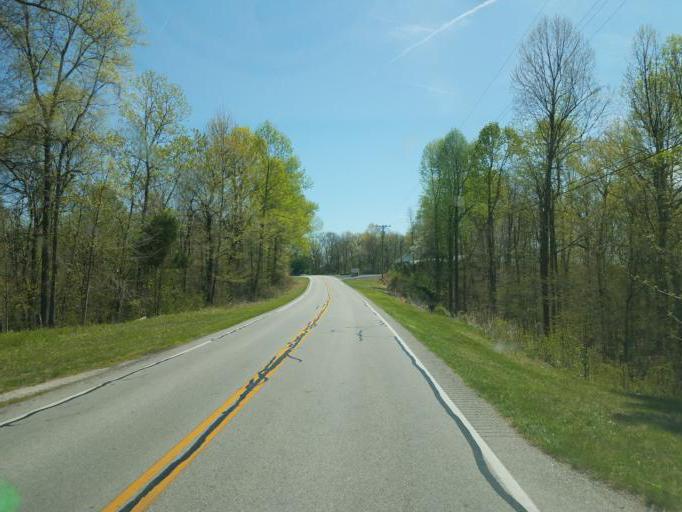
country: US
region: Kentucky
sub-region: Barren County
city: Cave City
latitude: 37.1317
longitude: -86.0301
